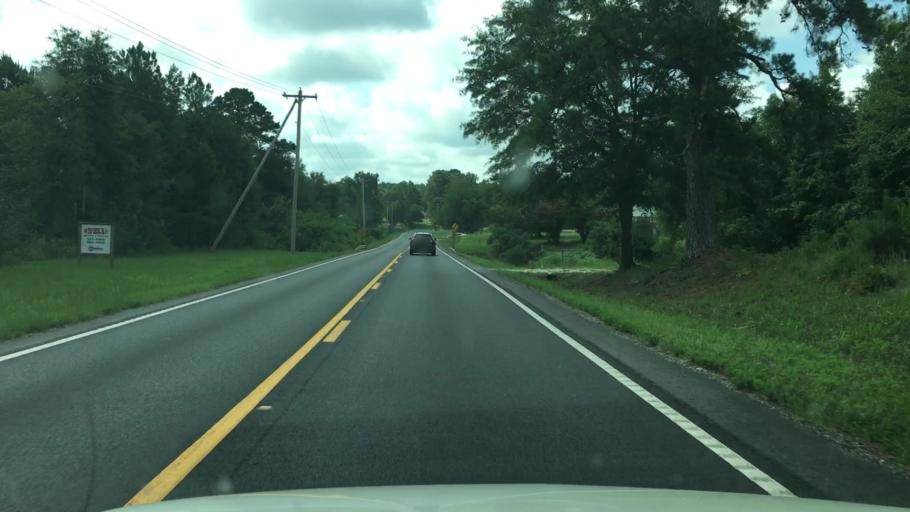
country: US
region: Arkansas
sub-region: Garland County
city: Lake Hamilton
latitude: 34.2979
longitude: -93.1636
